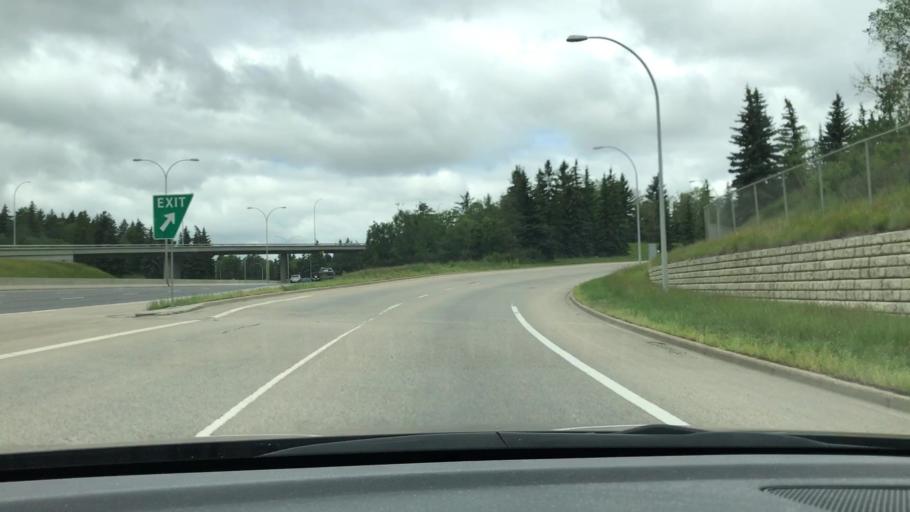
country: CA
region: Alberta
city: Edmonton
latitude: 53.5119
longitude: -113.5768
